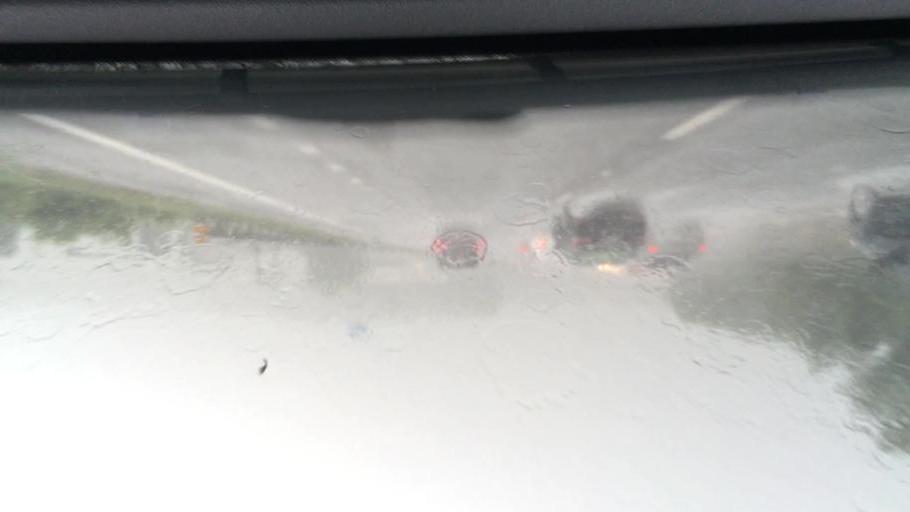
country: US
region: South Carolina
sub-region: Richland County
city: Columbia
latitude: 34.0659
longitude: -81.0406
